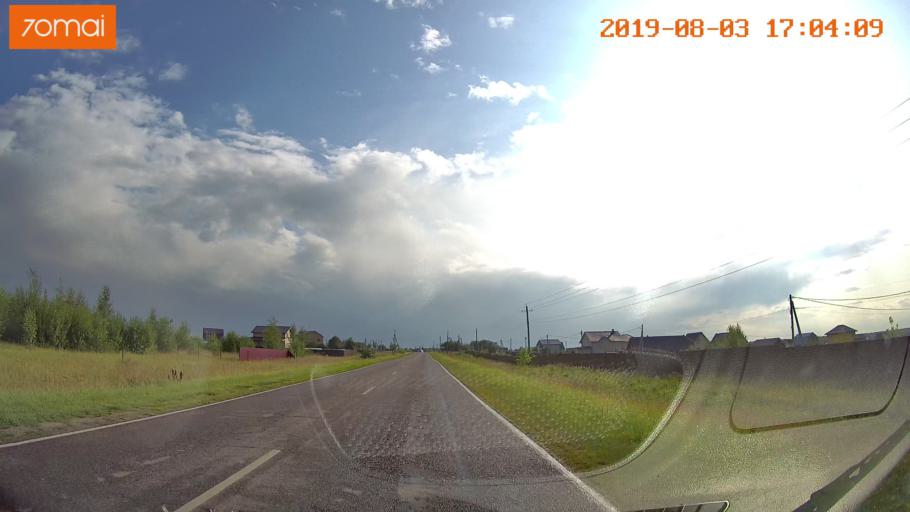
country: RU
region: Moskovskaya
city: Troitskoye
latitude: 55.3309
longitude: 38.5615
